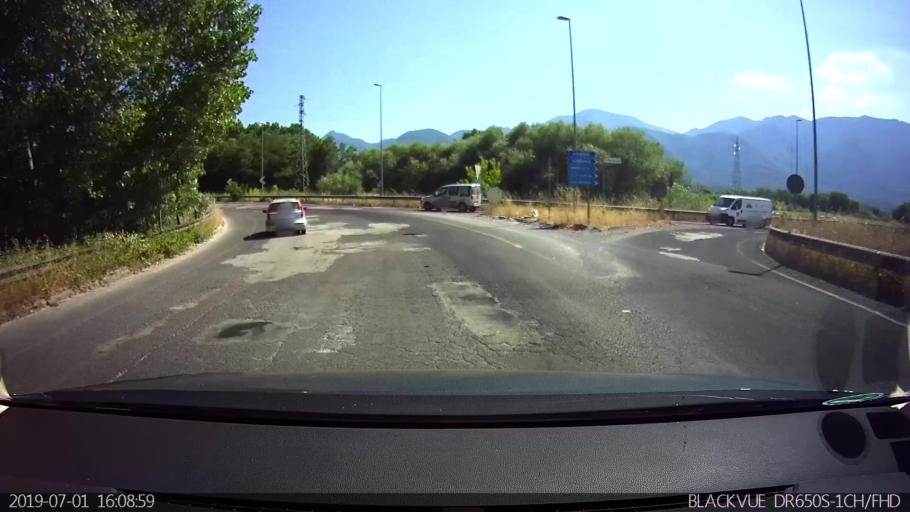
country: IT
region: Latium
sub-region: Provincia di Frosinone
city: Cartiera-Stazione
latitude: 41.6436
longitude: 13.2531
